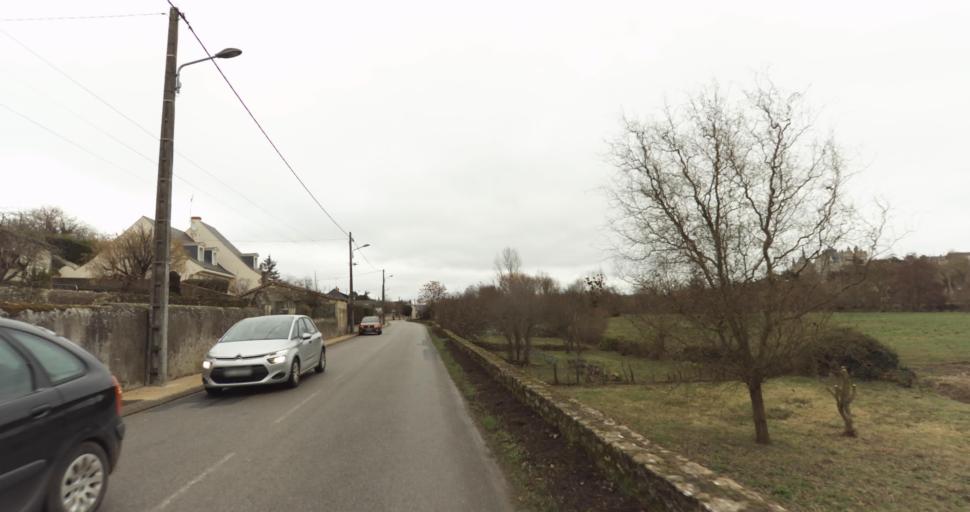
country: FR
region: Pays de la Loire
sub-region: Departement de Maine-et-Loire
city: Montreuil-Bellay
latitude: 47.1337
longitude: -0.1620
